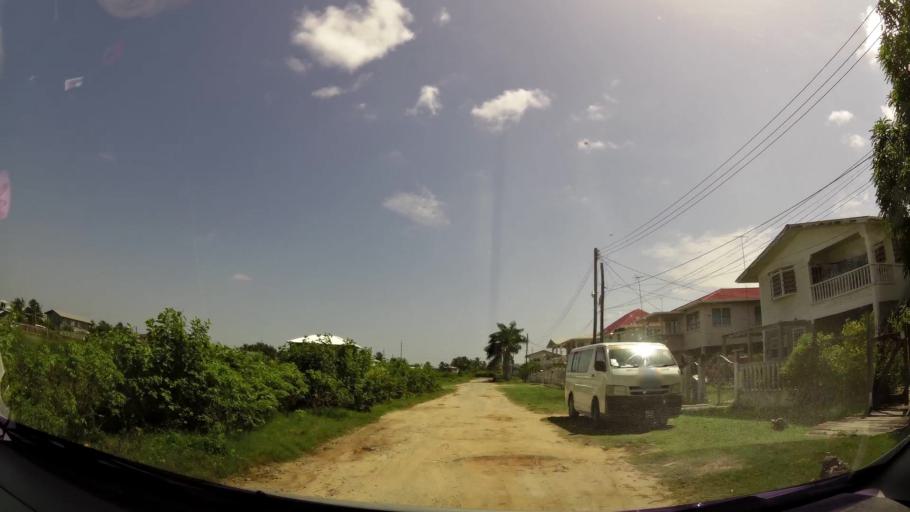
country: GY
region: Demerara-Mahaica
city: Mahaica Village
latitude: 6.7721
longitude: -58.0095
